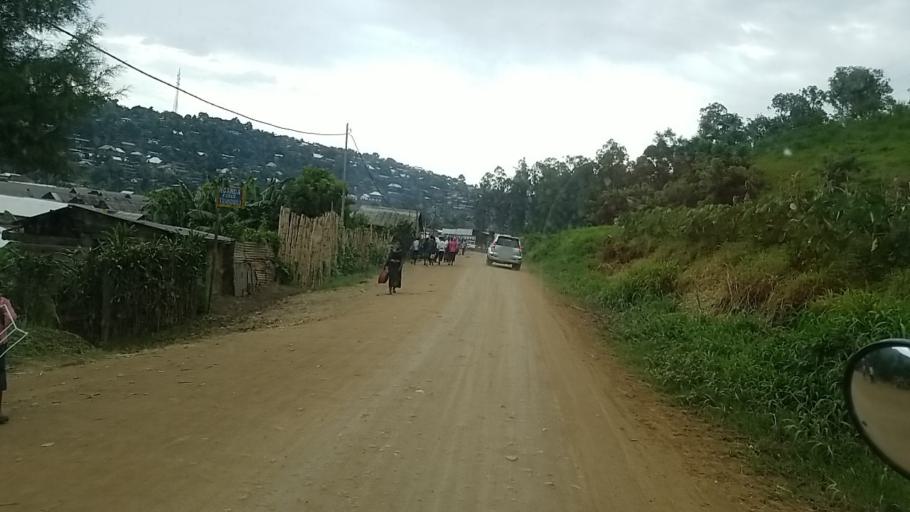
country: CD
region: Nord Kivu
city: Sake
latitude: -1.7052
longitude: 29.0185
